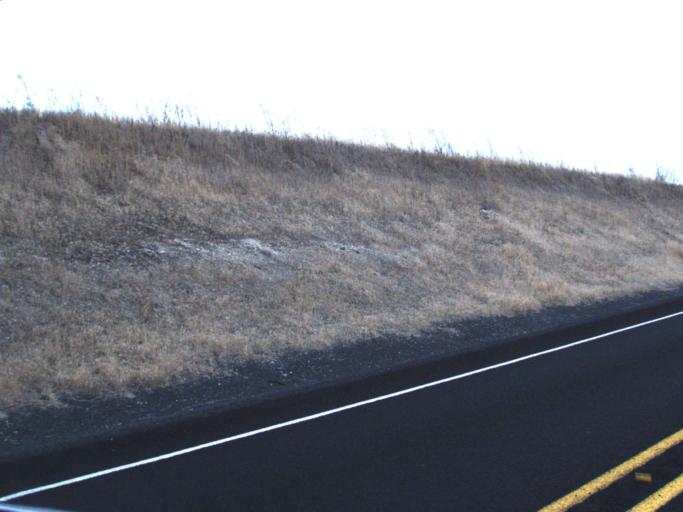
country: US
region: Washington
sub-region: Okanogan County
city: Coulee Dam
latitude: 47.8376
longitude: -118.7999
